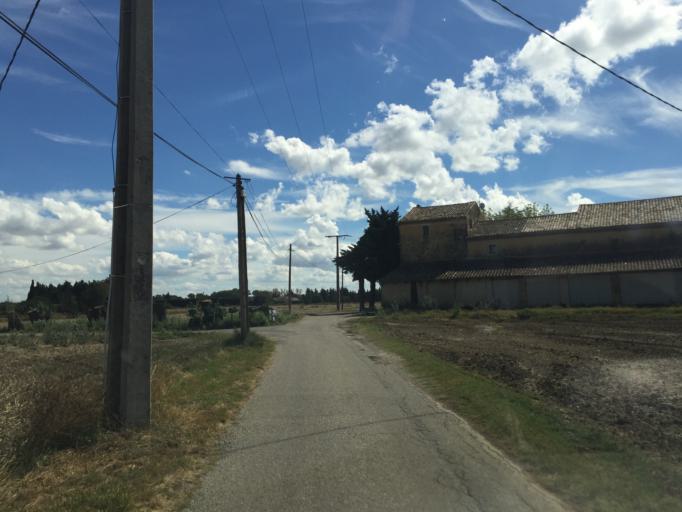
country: FR
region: Provence-Alpes-Cote d'Azur
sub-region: Departement du Vaucluse
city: Caderousse
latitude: 44.1230
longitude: 4.7366
